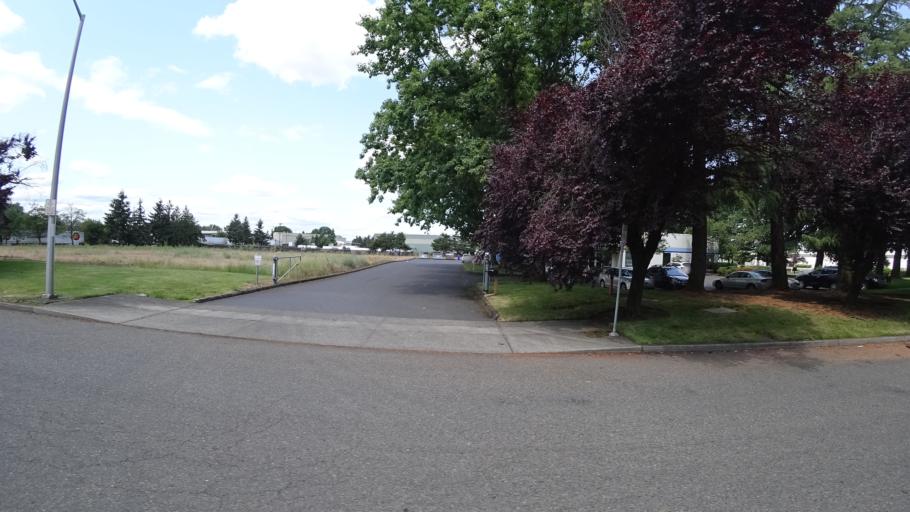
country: US
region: Oregon
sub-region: Washington County
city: West Haven
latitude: 45.6203
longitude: -122.7722
